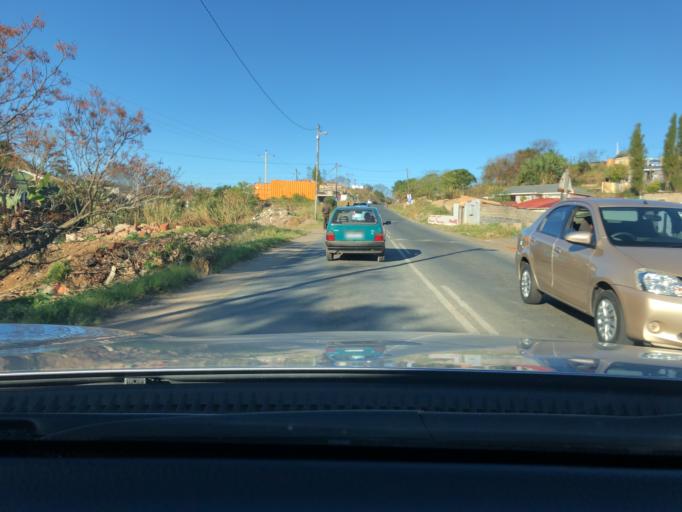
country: ZA
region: KwaZulu-Natal
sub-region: eThekwini Metropolitan Municipality
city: Umkomaas
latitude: -30.0362
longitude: 30.8676
